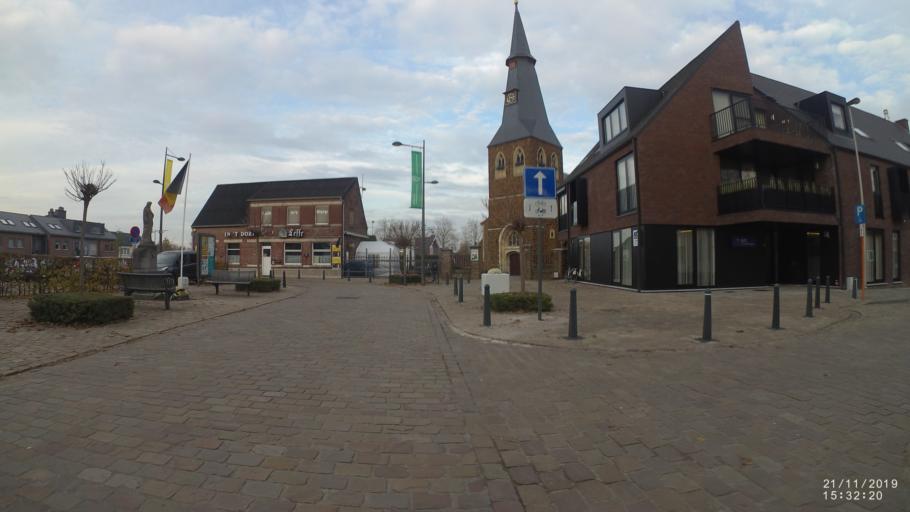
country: BE
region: Flanders
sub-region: Provincie Limburg
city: Hasselt
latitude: 50.9438
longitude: 5.3055
